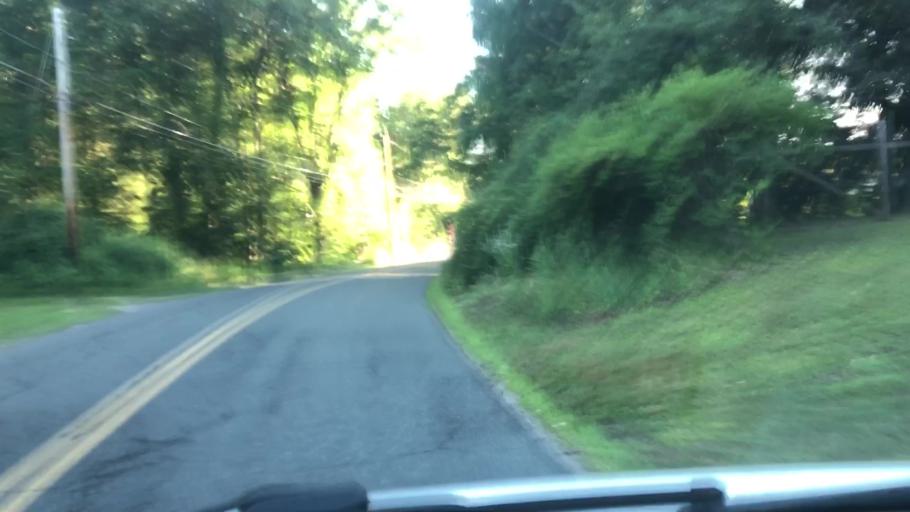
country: US
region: Massachusetts
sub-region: Hampshire County
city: Williamsburg
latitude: 42.3783
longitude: -72.7312
